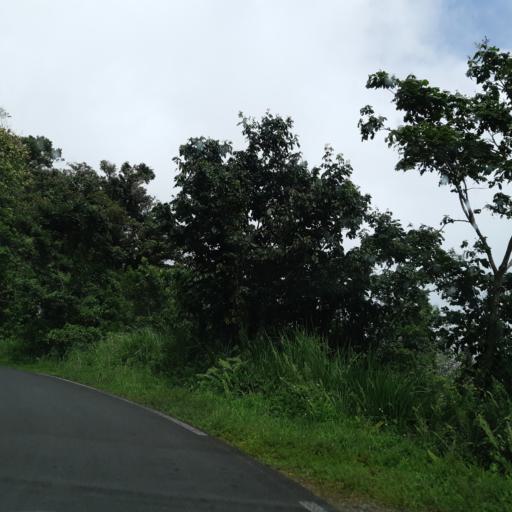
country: GP
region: Guadeloupe
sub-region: Guadeloupe
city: Saint-Claude
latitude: 16.0312
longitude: -61.6808
